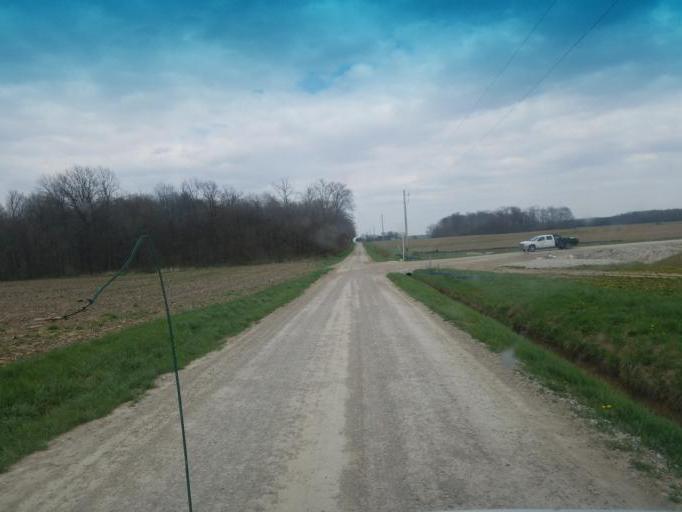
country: US
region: Ohio
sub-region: Crawford County
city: Bucyrus
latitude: 40.9793
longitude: -82.9697
